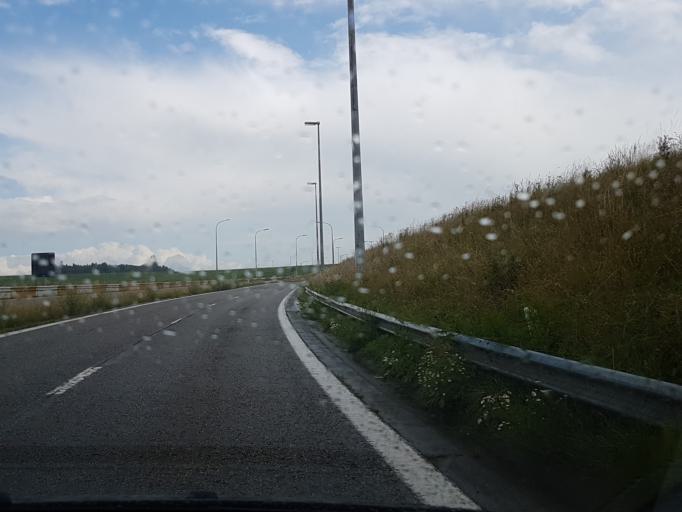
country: BE
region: Flanders
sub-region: Provincie Vlaams-Brabant
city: Bever
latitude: 50.9048
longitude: 4.3263
